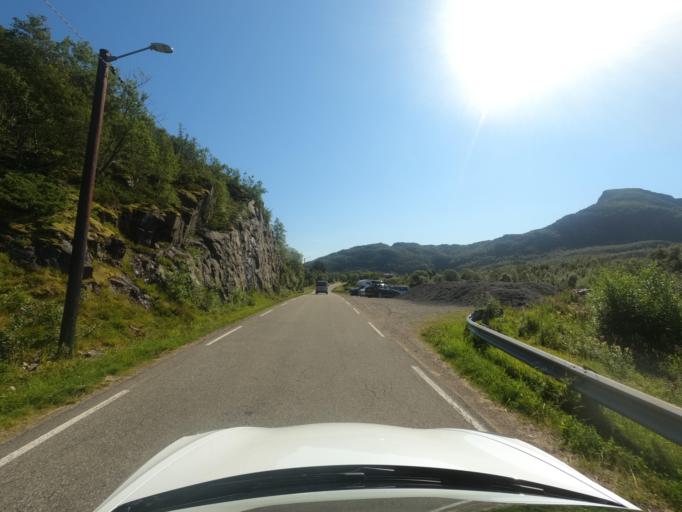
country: NO
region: Nordland
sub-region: Hadsel
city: Stokmarknes
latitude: 68.3041
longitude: 15.0108
